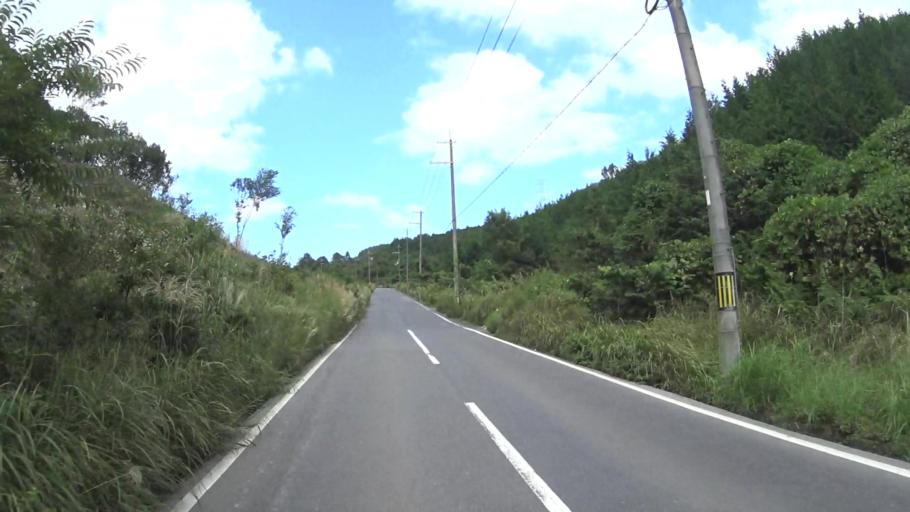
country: JP
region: Shiga Prefecture
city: Otsu-shi
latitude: 34.9268
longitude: 135.8867
